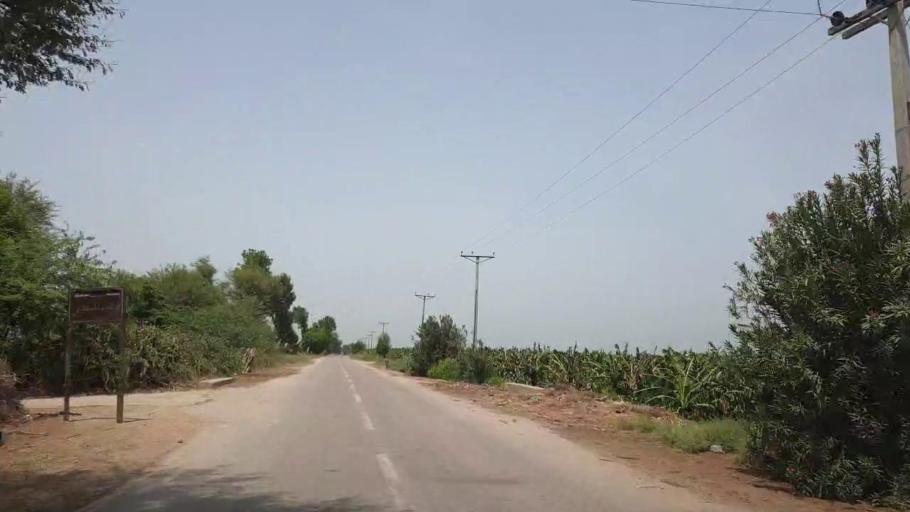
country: PK
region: Sindh
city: Sakrand
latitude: 26.1775
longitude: 68.2272
